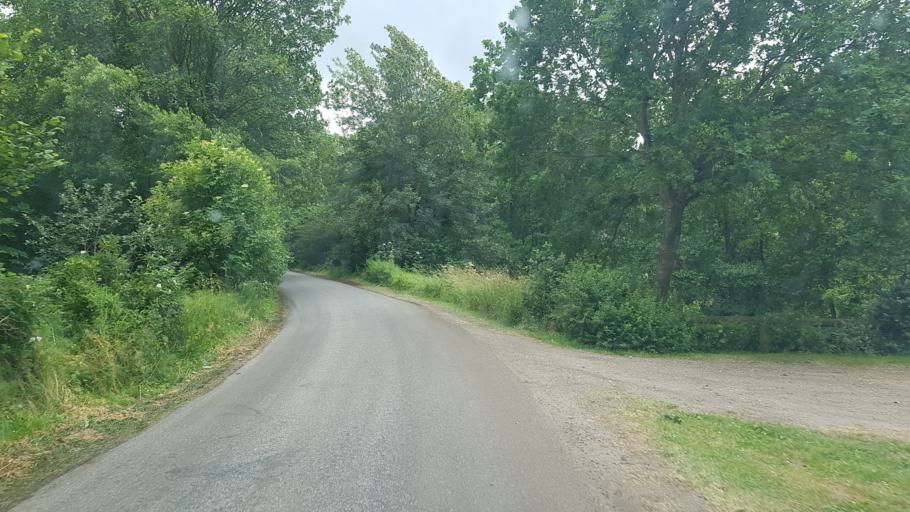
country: DK
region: South Denmark
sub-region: Kolding Kommune
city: Lunderskov
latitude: 55.4992
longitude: 9.3027
